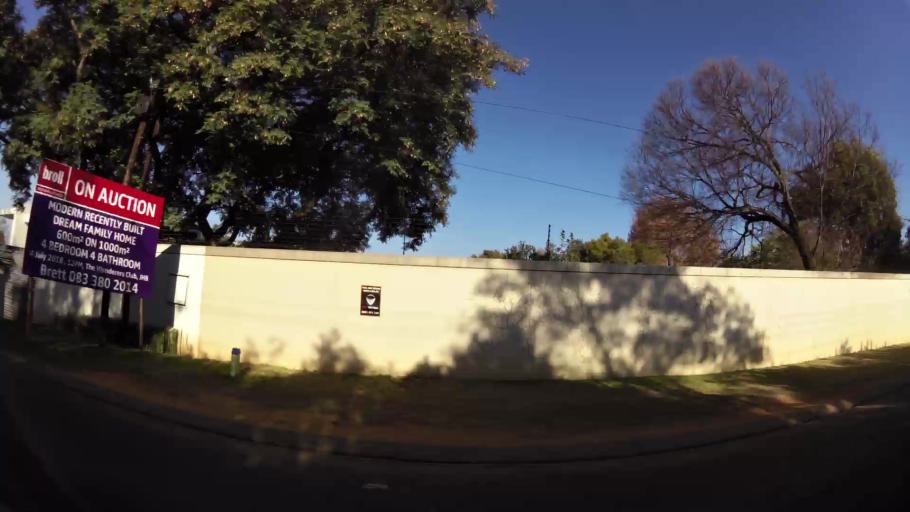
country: ZA
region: Gauteng
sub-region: City of Johannesburg Metropolitan Municipality
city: Johannesburg
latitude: -26.1149
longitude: 28.0649
